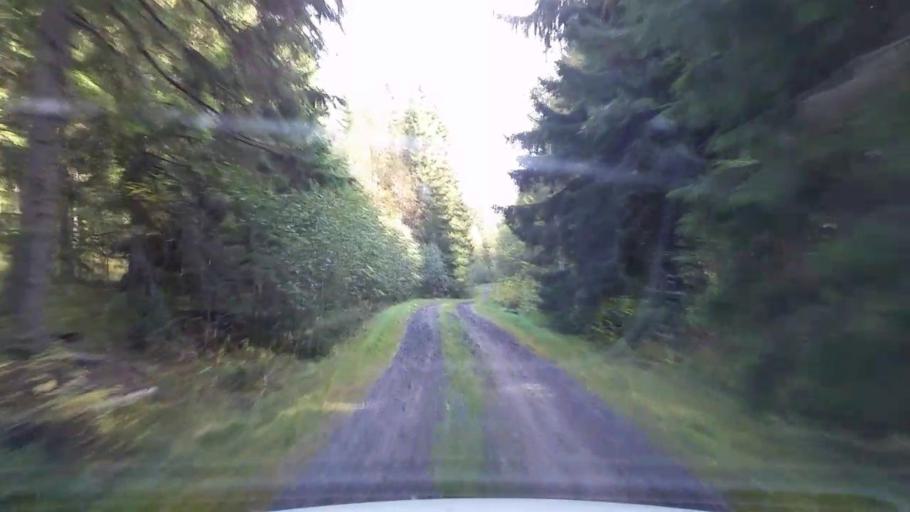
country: SE
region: Gaevleborg
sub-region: Ljusdals Kommun
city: Jaervsoe
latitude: 61.7807
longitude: 16.1784
